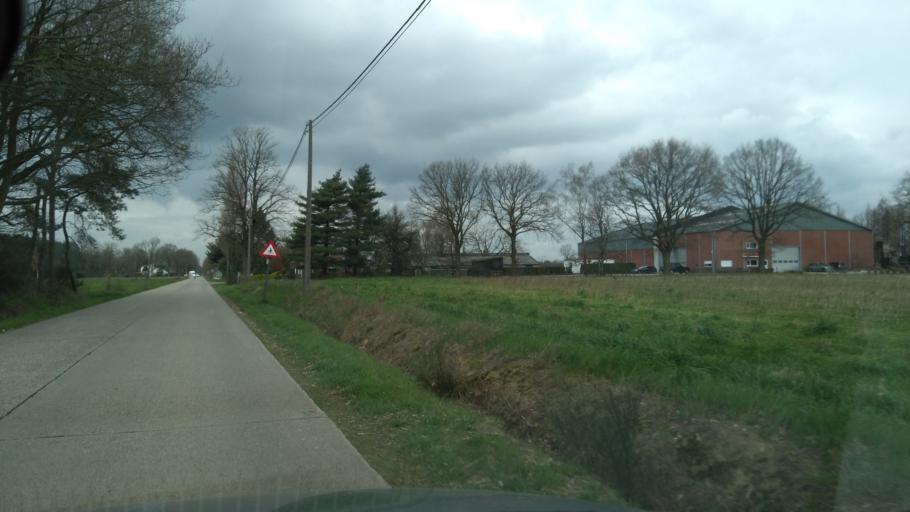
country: BE
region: Flanders
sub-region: Provincie Antwerpen
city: Ravels
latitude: 51.4132
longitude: 4.9801
